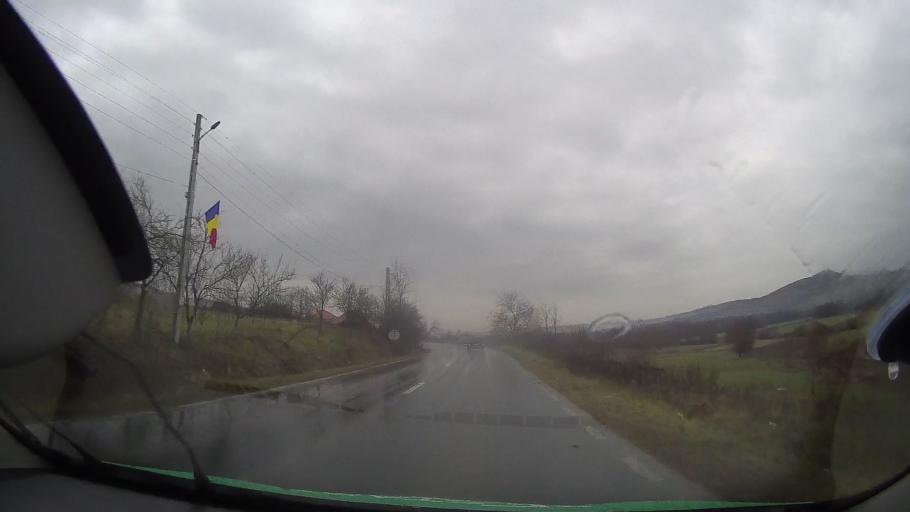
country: RO
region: Bihor
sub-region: Comuna Rabagani
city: Rabagani
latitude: 46.7577
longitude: 22.2021
